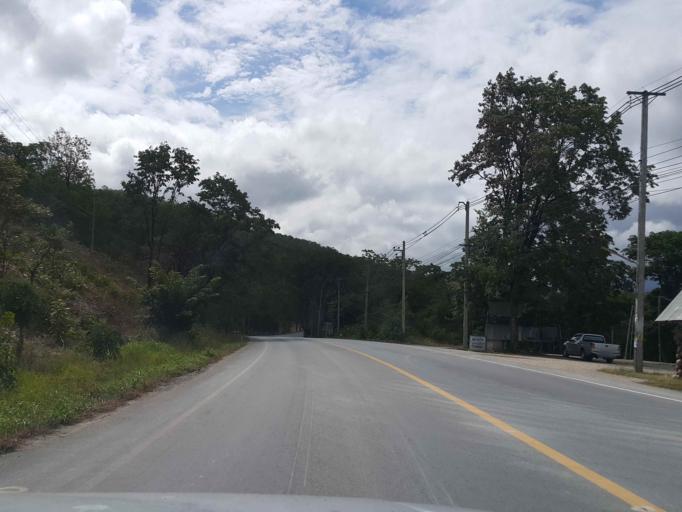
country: TH
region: Tak
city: Tak
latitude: 16.8019
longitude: 99.0008
